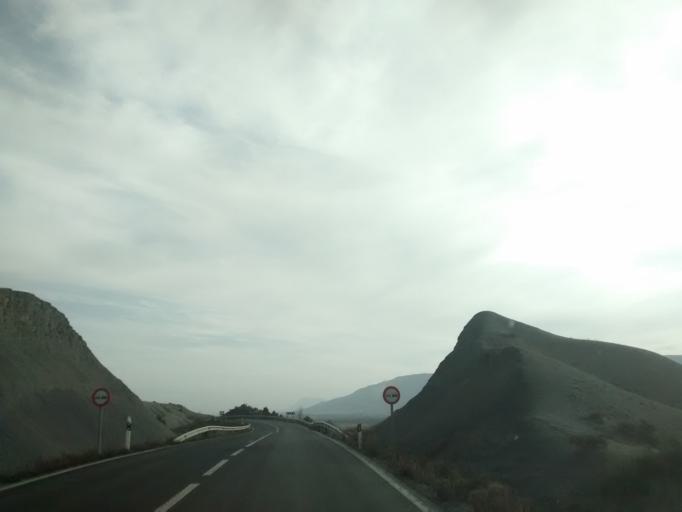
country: ES
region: Aragon
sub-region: Provincia de Zaragoza
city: Siguees
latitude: 42.6149
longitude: -1.0712
